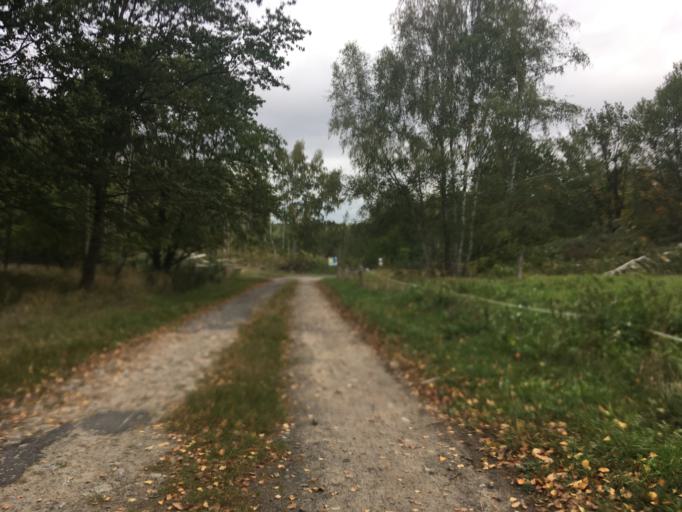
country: DE
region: Brandenburg
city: Dallgow-Doeberitz
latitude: 52.5269
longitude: 13.0783
